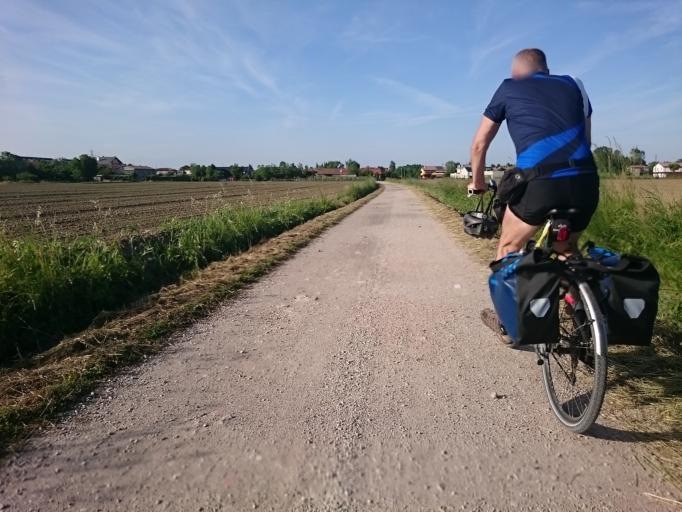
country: IT
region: Veneto
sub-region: Provincia di Padova
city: Mandriola-Sant'Agostino
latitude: 45.3637
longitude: 11.8313
